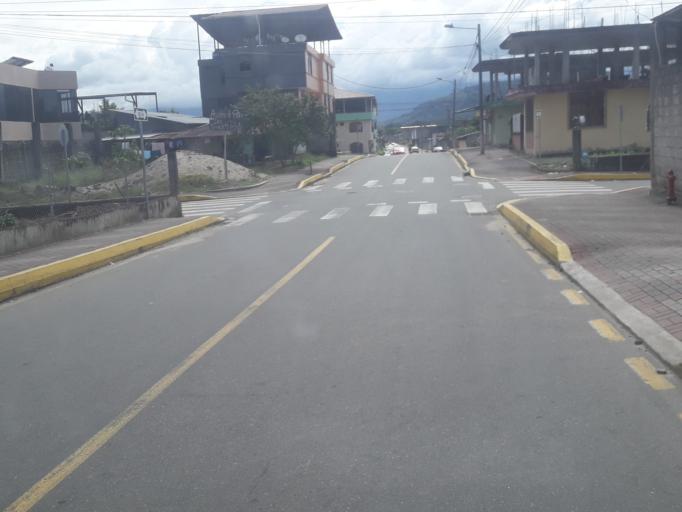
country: EC
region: Napo
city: Tena
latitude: -1.0069
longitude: -77.8135
